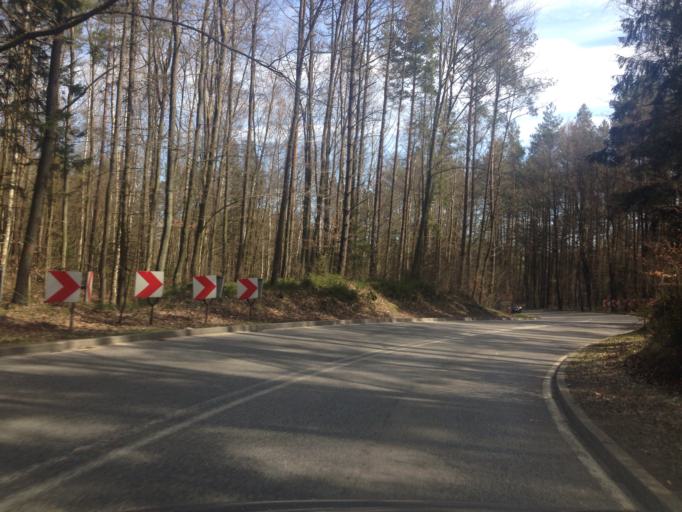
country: PL
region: Pomeranian Voivodeship
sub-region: Gdynia
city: Wielki Kack
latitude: 54.4774
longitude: 18.4530
